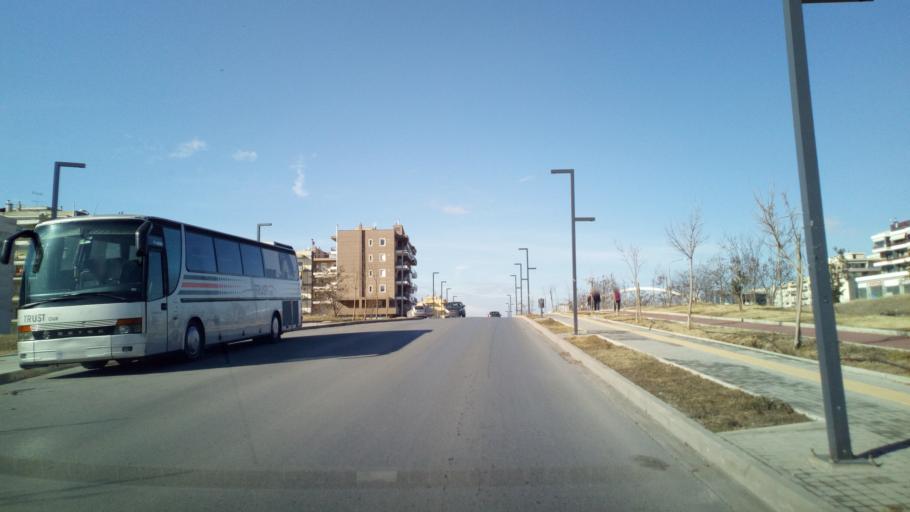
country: GR
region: Central Macedonia
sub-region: Nomos Thessalonikis
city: Evosmos
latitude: 40.6773
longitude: 22.9176
